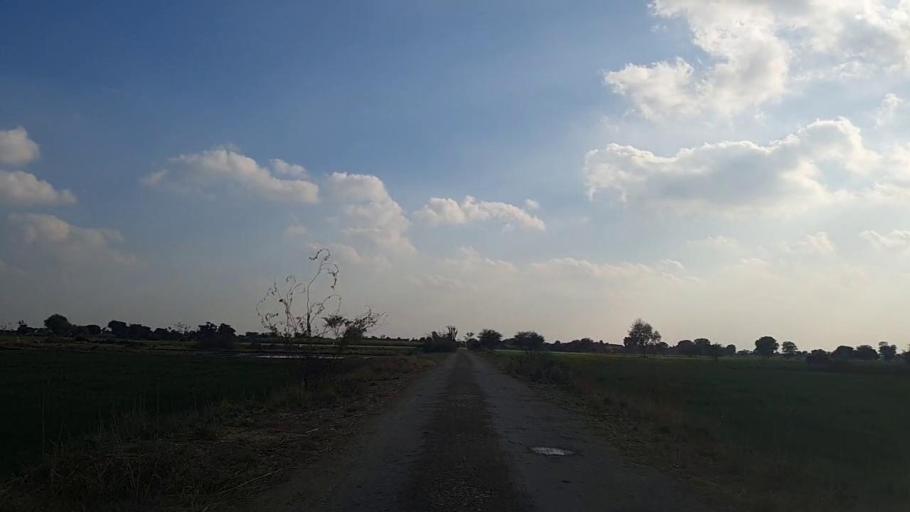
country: PK
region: Sindh
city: Tando Mittha Khan
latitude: 25.9429
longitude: 69.2149
